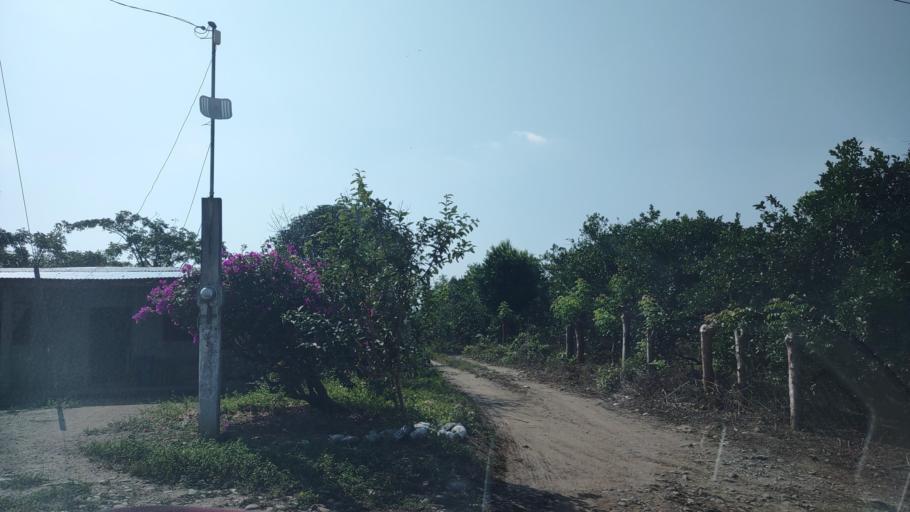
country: MX
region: Puebla
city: Espinal
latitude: 20.2402
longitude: -97.3459
